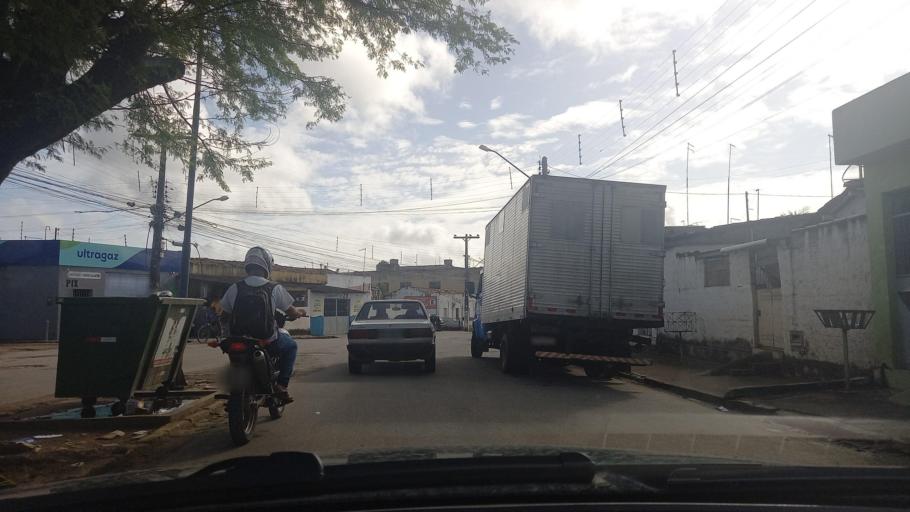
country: BR
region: Pernambuco
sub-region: Vitoria De Santo Antao
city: Vitoria de Santo Antao
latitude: -8.1023
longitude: -35.2831
